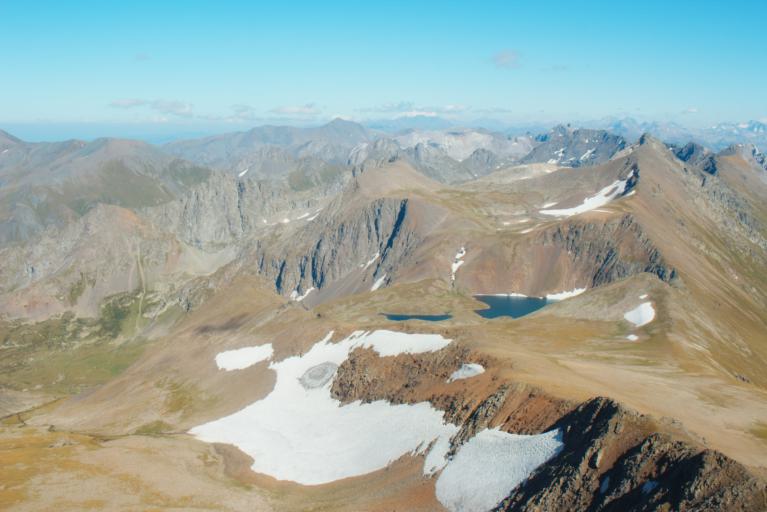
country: RU
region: Karachayevo-Cherkesiya
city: Mednogorskiy
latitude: 43.6208
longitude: 41.0907
